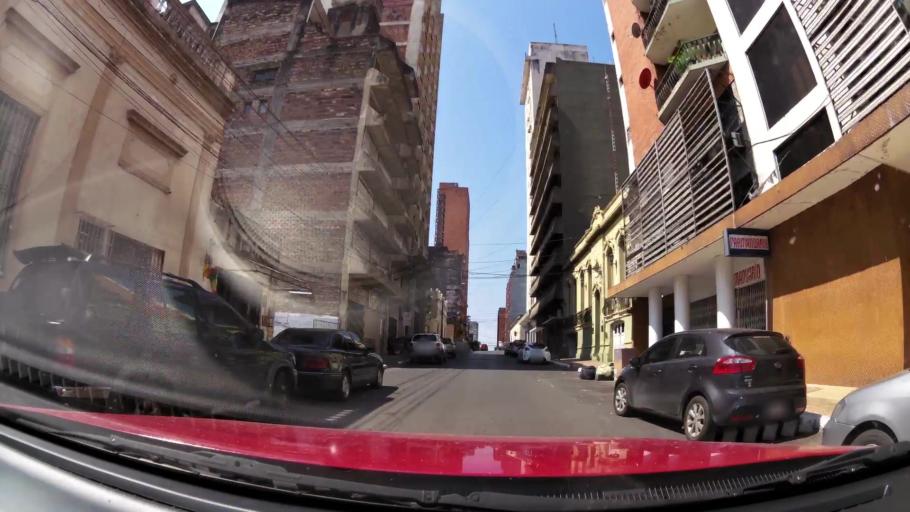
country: PY
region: Asuncion
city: Asuncion
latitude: -25.2826
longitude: -57.6403
